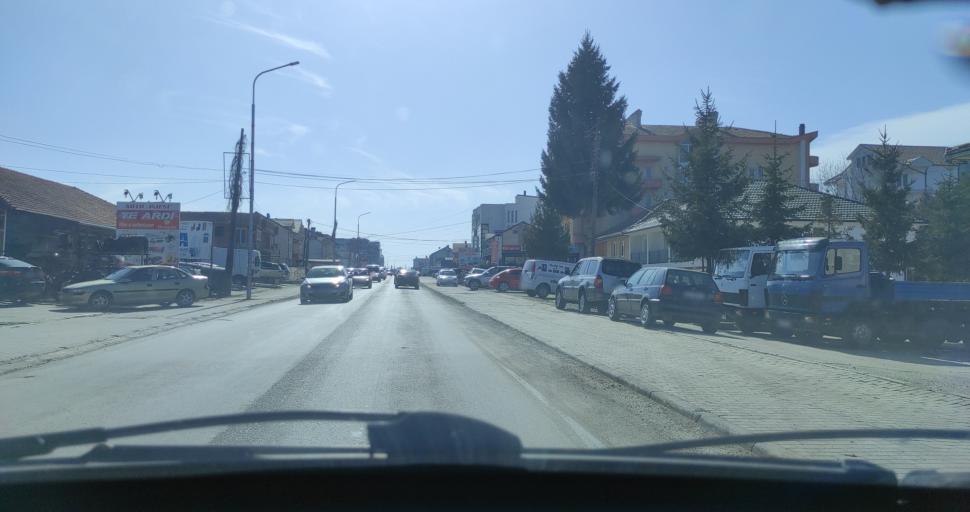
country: XK
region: Gjakova
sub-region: Komuna e Decanit
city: Decan
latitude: 42.5482
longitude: 20.2904
